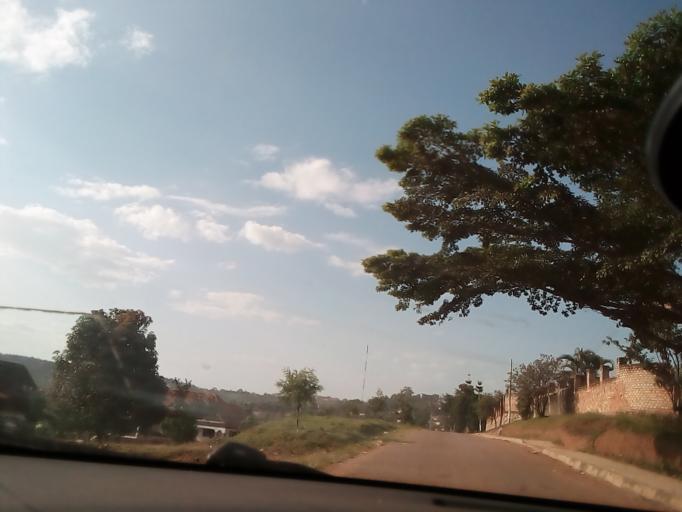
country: UG
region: Central Region
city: Masaka
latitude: -0.3518
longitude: 31.7432
